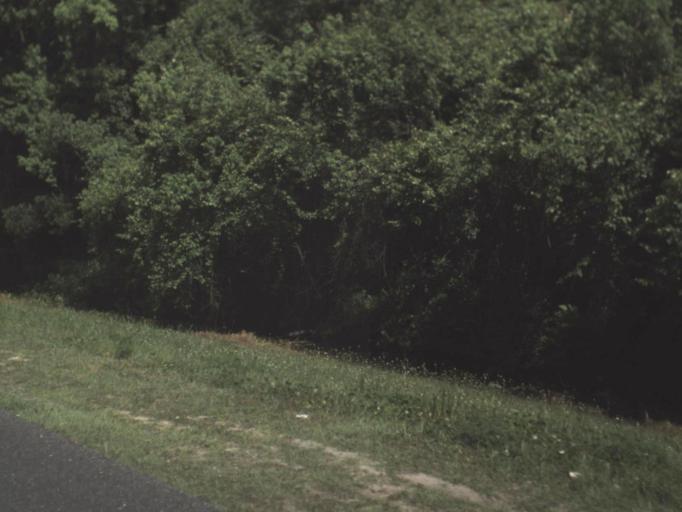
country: US
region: Florida
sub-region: Duval County
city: Jacksonville
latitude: 30.4069
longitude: -81.6552
